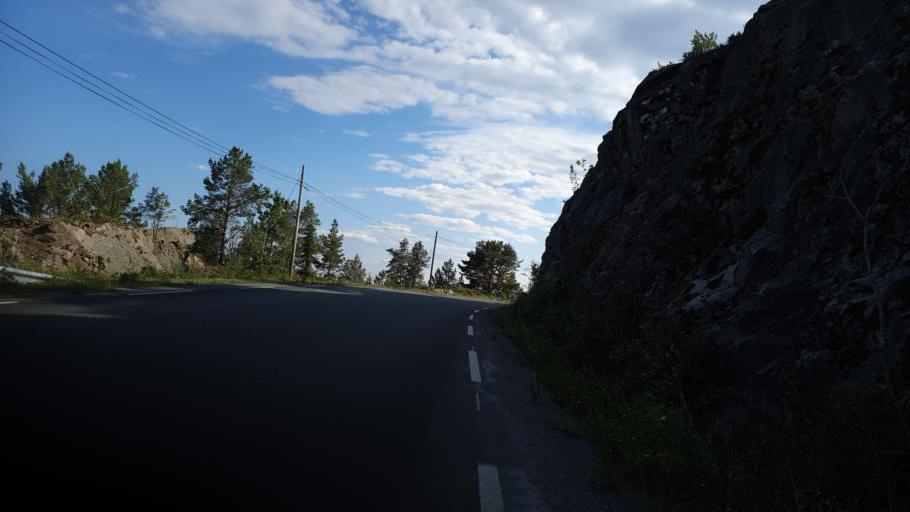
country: NO
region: Sor-Trondelag
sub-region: Trondheim
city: Trondheim
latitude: 63.5681
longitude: 10.3418
